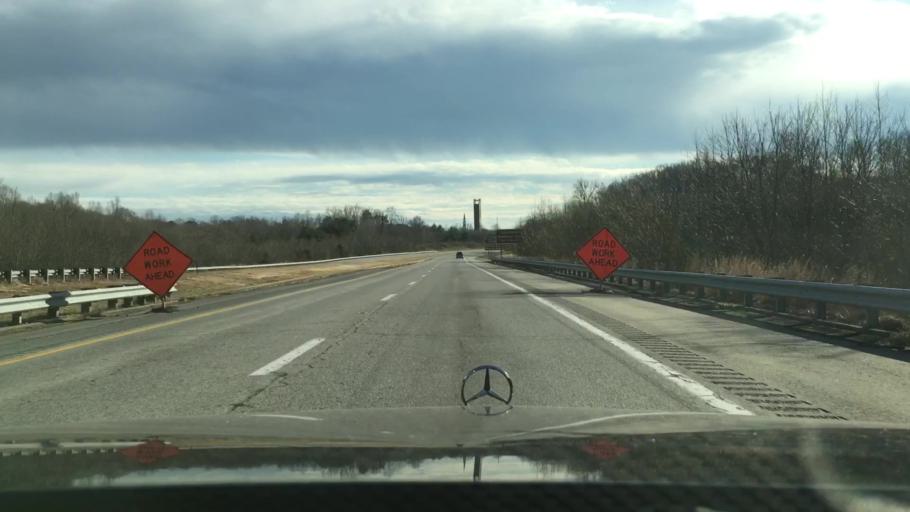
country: US
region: Virginia
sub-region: City of Danville
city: Danville
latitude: 36.5944
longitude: -79.3570
